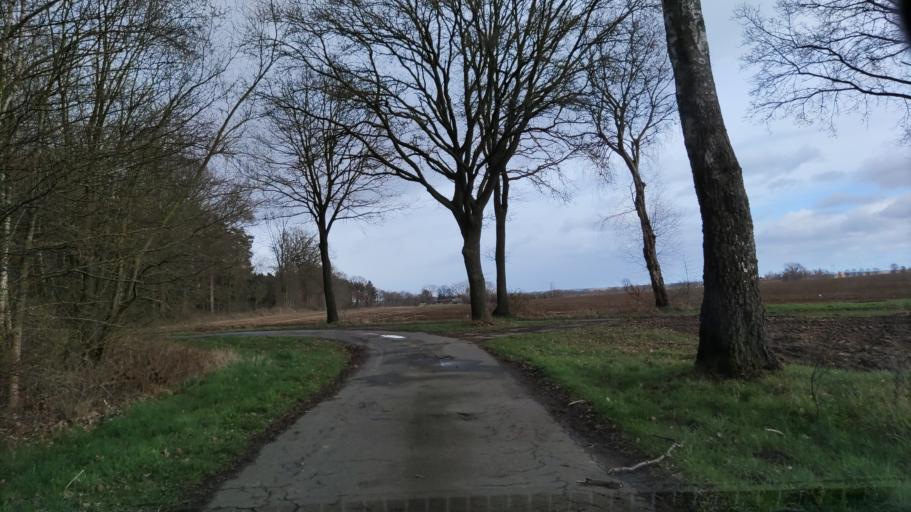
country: DE
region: Lower Saxony
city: Thomasburg
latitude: 53.1988
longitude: 10.6890
